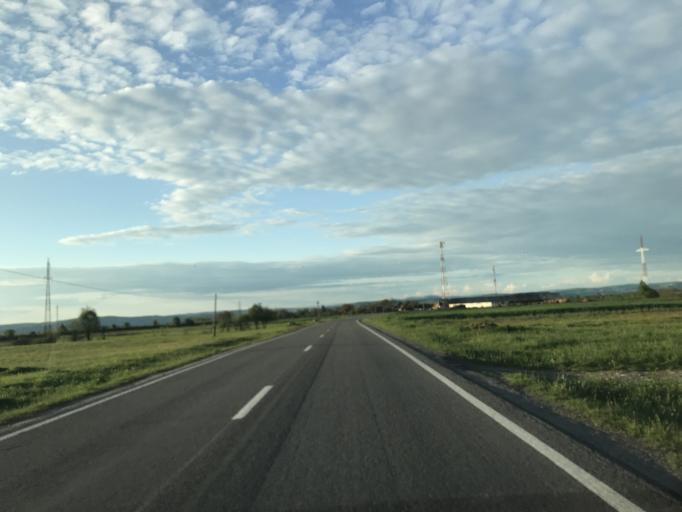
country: RO
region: Sibiu
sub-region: Comuna Cartisoara
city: Cartisoara
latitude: 45.7169
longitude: 24.5696
